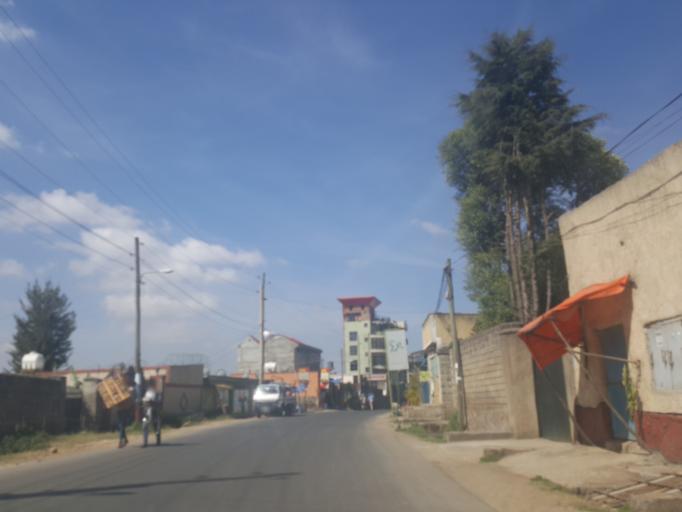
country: ET
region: Adis Abeba
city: Addis Ababa
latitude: 9.0641
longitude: 38.7260
